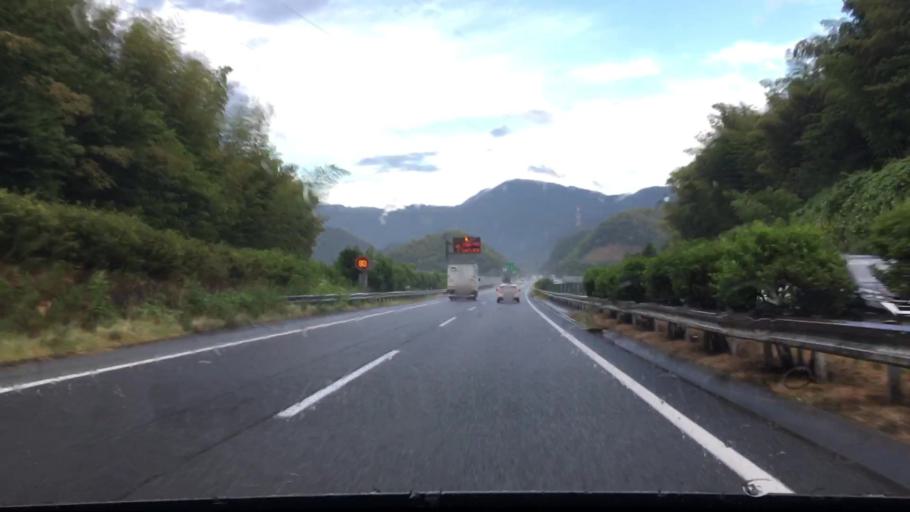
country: JP
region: Fukuoka
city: Kitakyushu
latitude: 33.8064
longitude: 130.8465
